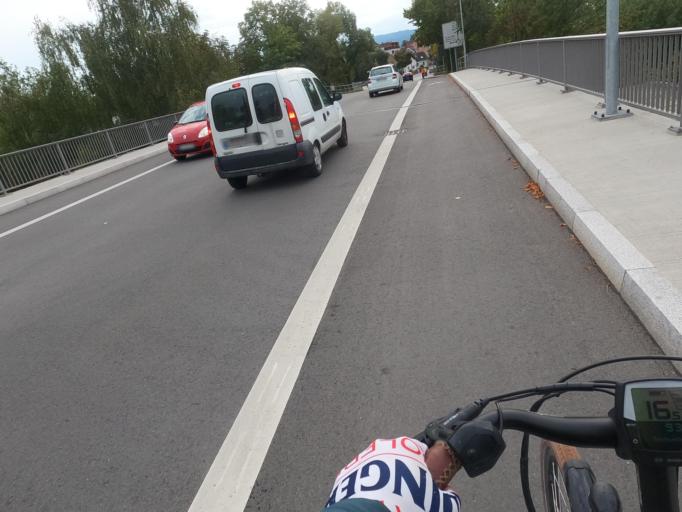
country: DE
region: Baden-Wuerttemberg
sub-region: Freiburg Region
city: Radolfzell am Bodensee
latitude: 47.7404
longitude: 8.9771
